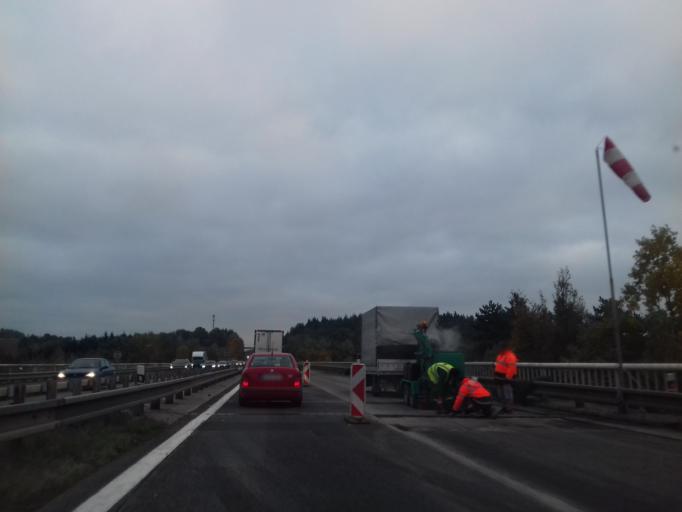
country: CZ
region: Central Bohemia
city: Ondrejov
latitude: 49.9010
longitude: 14.7391
